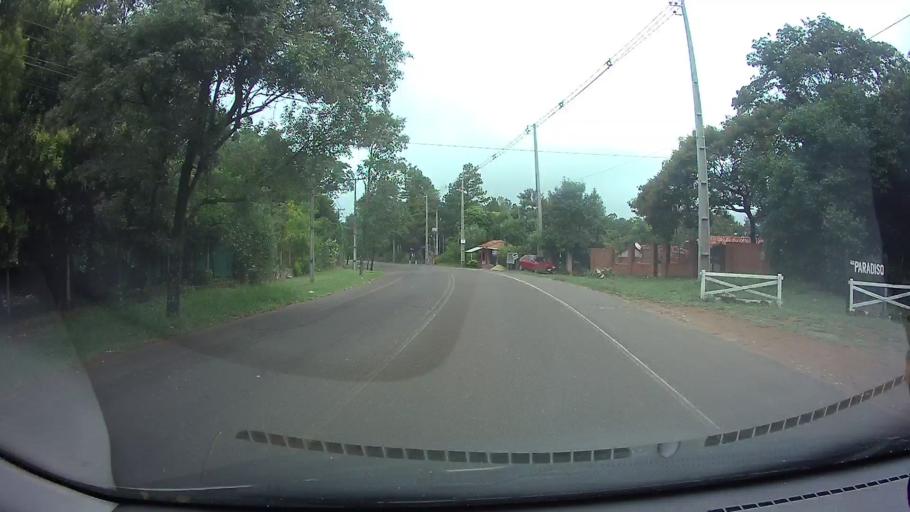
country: PY
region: Cordillera
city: Altos
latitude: -25.2902
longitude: -57.2683
